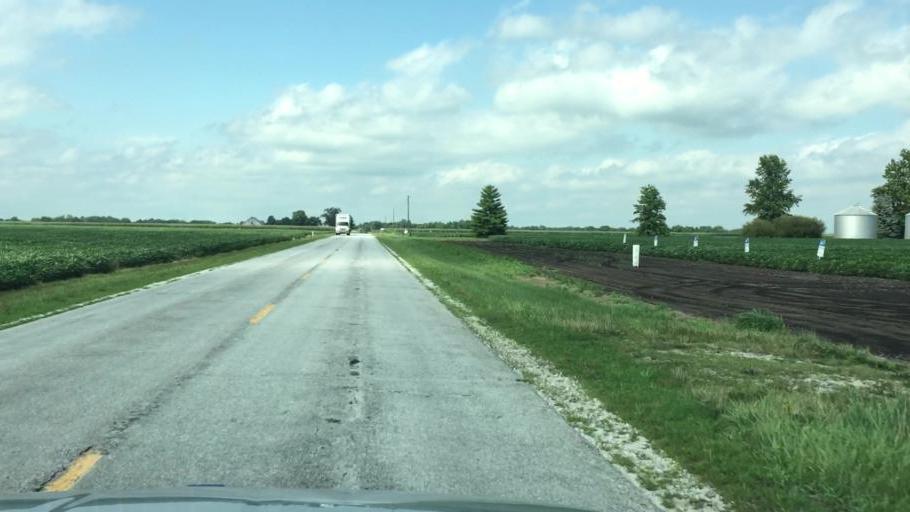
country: US
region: Illinois
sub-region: Hancock County
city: Nauvoo
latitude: 40.5109
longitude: -91.3083
